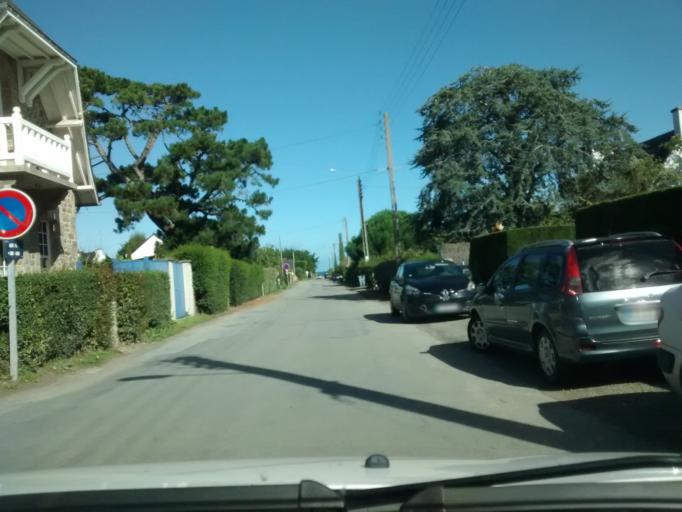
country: FR
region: Brittany
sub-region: Departement d'Ille-et-Vilaine
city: Saint-Briac-sur-Mer
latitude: 48.6279
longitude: -2.1416
